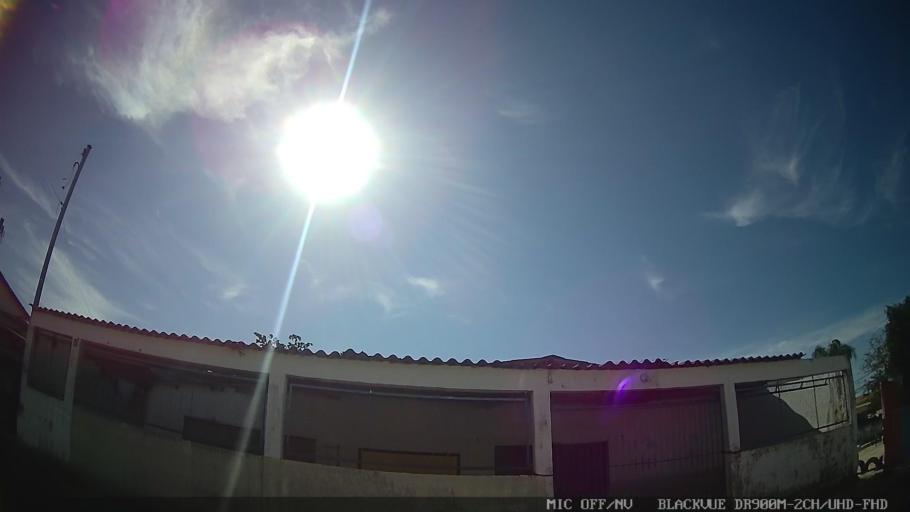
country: BR
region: Sao Paulo
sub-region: Santos
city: Santos
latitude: -23.9409
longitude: -46.2820
